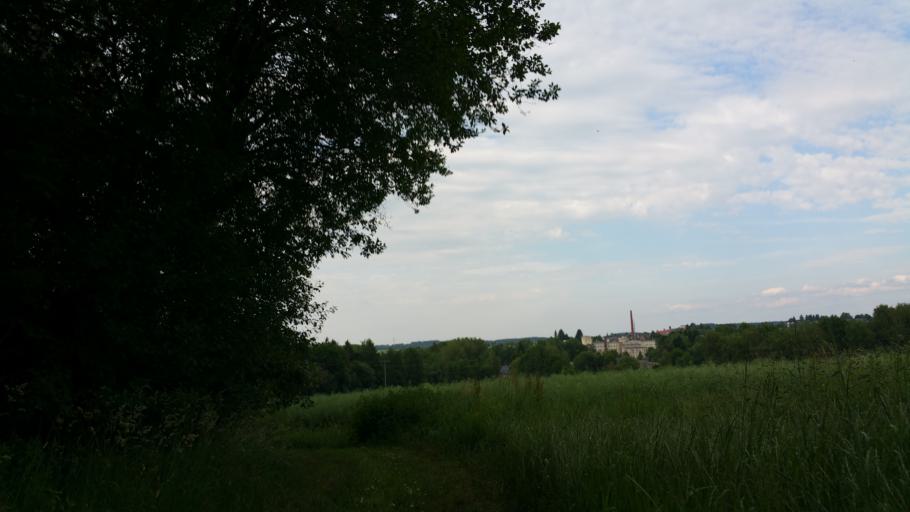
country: DE
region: Bavaria
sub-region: Upper Franconia
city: Schwarzenbach an der Saale
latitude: 50.2133
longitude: 11.9253
